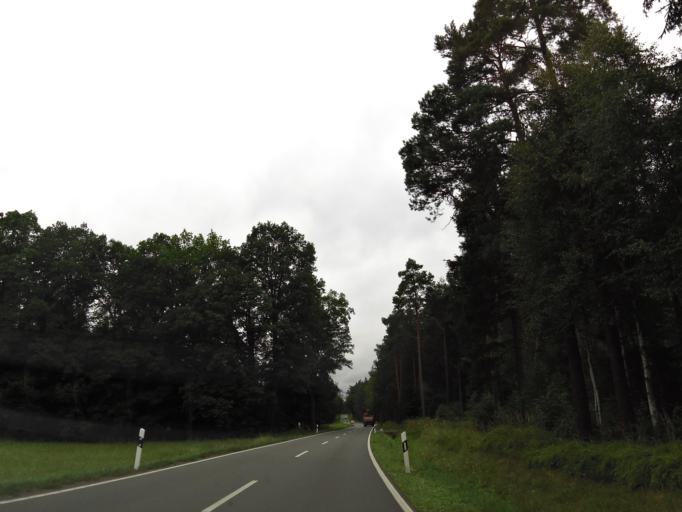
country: DE
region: Thuringia
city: Bad Klosterlausnitz
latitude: 50.9300
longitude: 11.8619
